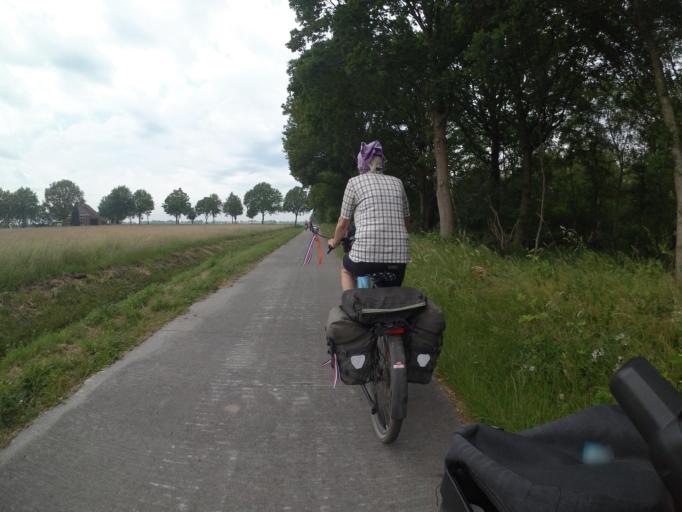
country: NL
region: Drenthe
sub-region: Gemeente Assen
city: Assen
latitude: 52.9980
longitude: 6.4602
